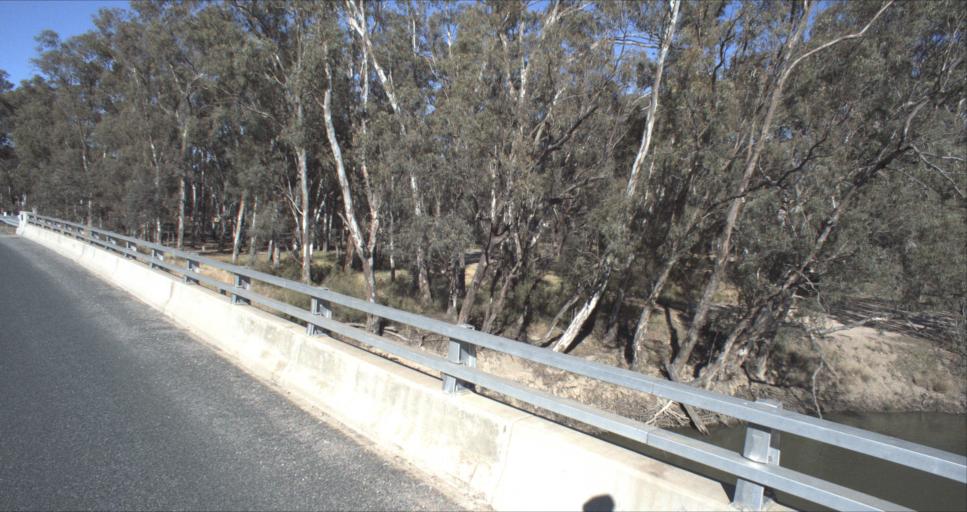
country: AU
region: New South Wales
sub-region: Leeton
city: Leeton
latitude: -34.6387
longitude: 146.3739
